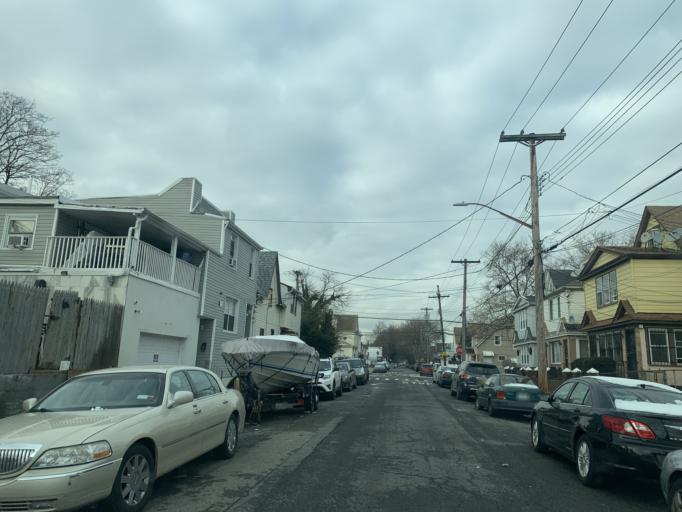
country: US
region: New York
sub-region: Queens County
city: Jamaica
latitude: 40.6885
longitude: -73.7946
